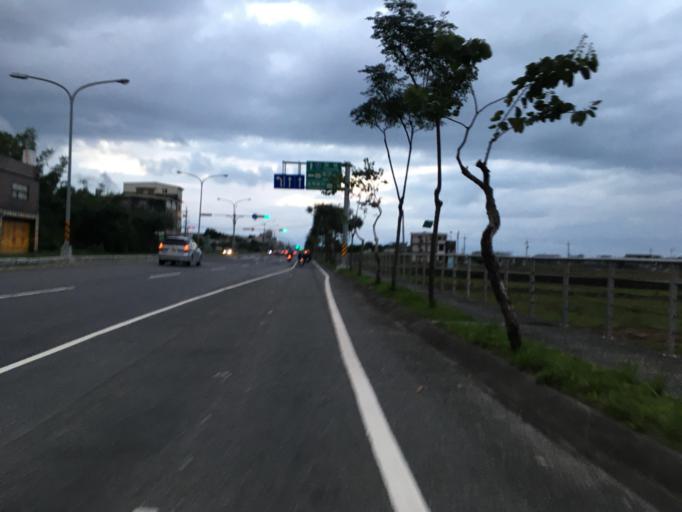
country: TW
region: Taiwan
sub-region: Yilan
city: Yilan
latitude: 24.6185
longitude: 121.8447
